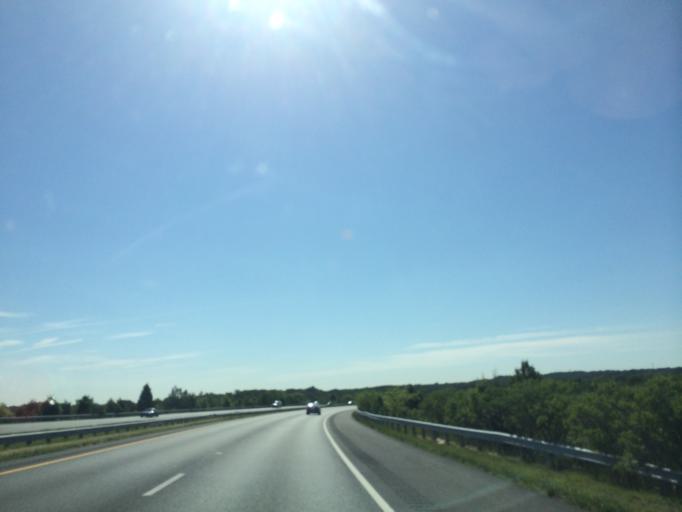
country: US
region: Maryland
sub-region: Anne Arundel County
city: Odenton
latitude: 39.1016
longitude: -76.6985
